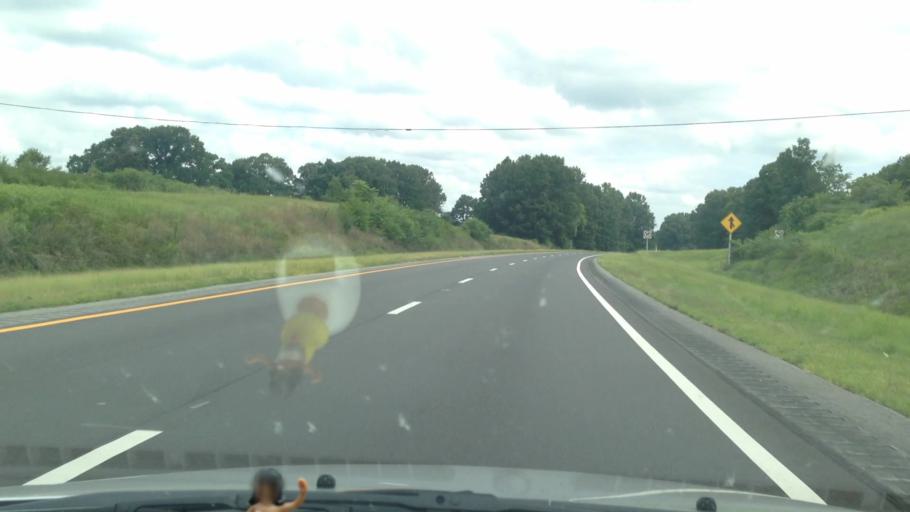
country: US
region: Virginia
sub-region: Pittsylvania County
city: Gretna
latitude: 36.9549
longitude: -79.3785
